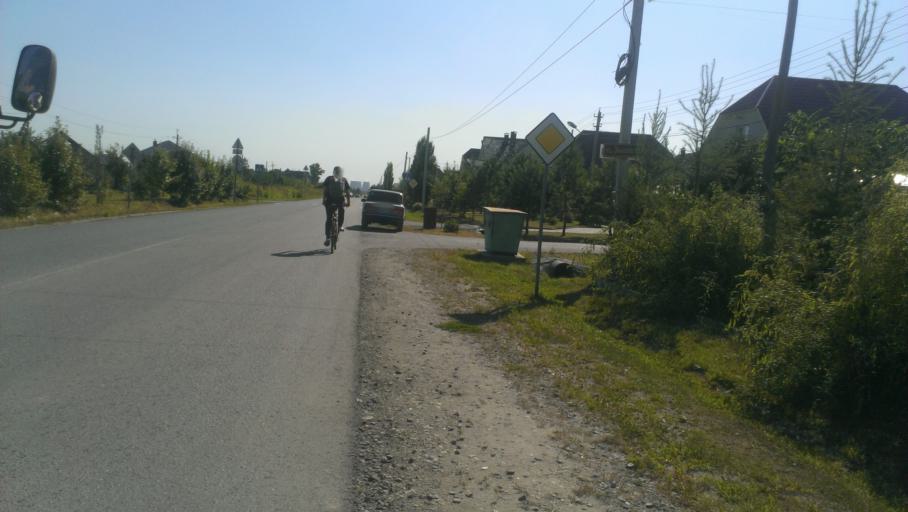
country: RU
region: Altai Krai
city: Novosilikatnyy
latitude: 53.3688
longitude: 83.6499
